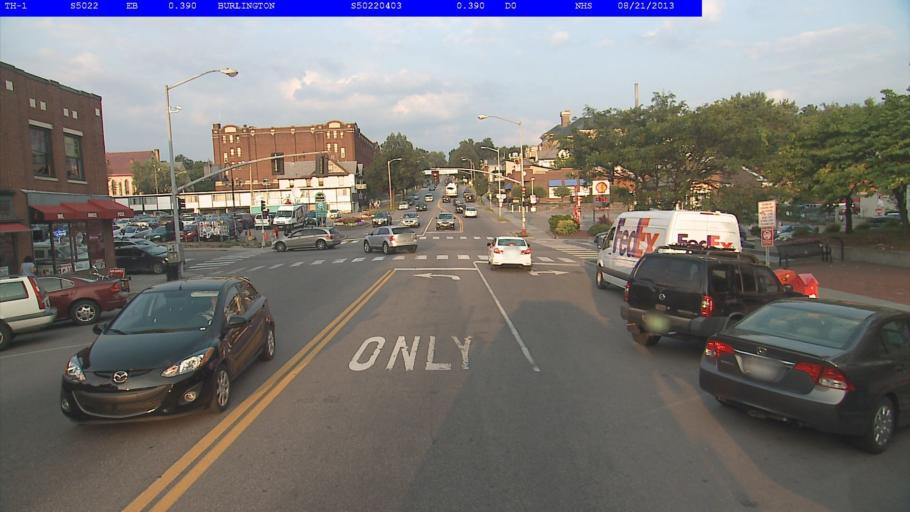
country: US
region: Vermont
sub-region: Chittenden County
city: Burlington
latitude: 44.4760
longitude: -73.2115
